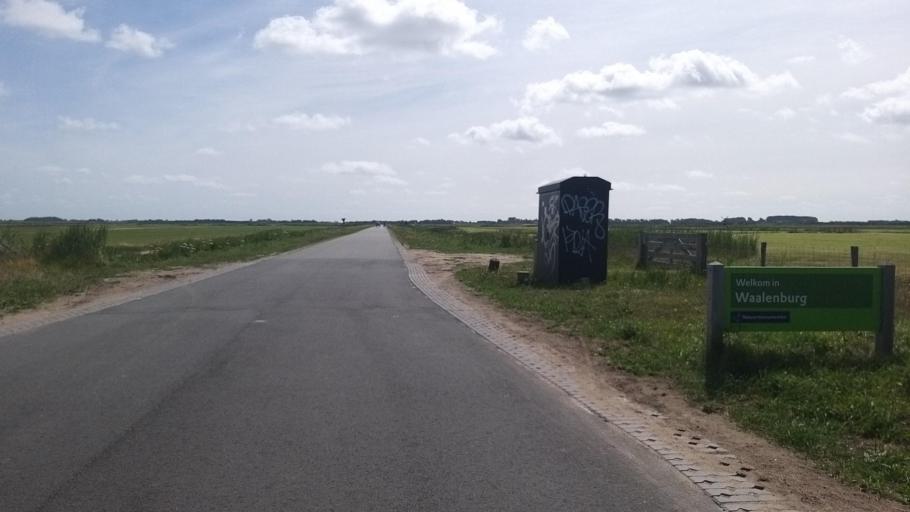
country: NL
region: North Holland
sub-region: Gemeente Texel
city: Den Burg
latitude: 53.0850
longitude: 4.7919
